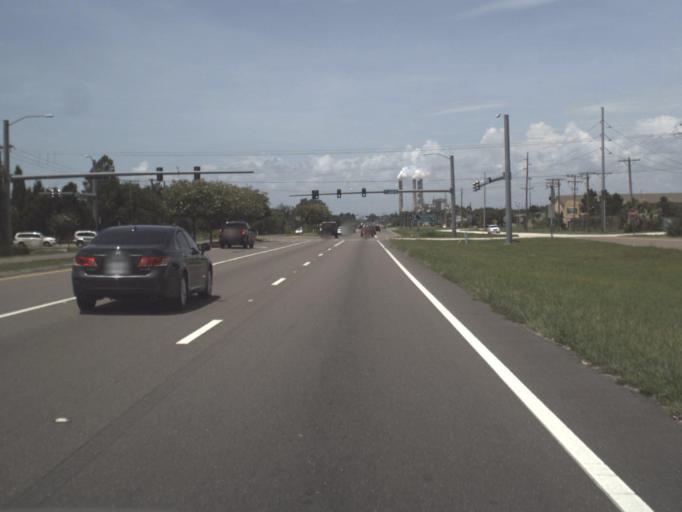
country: US
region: Florida
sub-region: Hillsborough County
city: Apollo Beach
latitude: 27.7921
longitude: -82.3666
